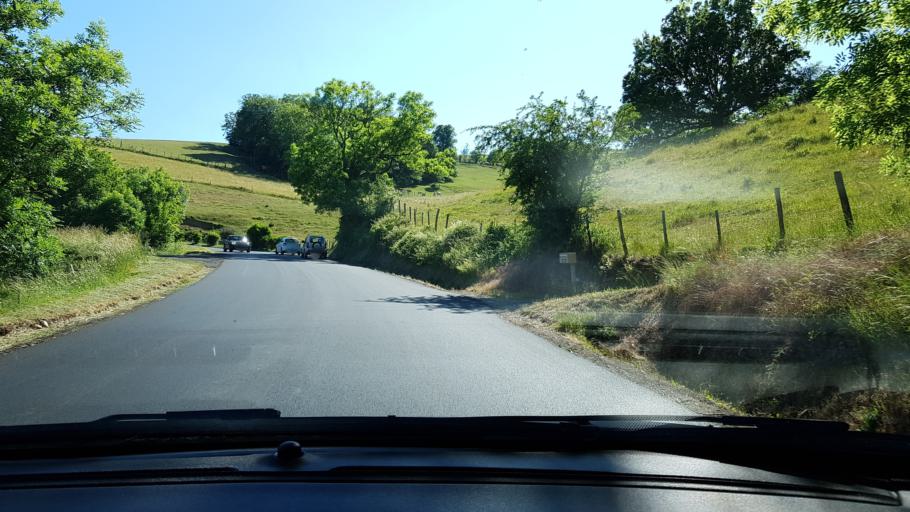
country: FR
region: Rhone-Alpes
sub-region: Departement du Rhone
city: Saint-Didier-sous-Riverie
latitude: 45.5996
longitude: 4.5973
